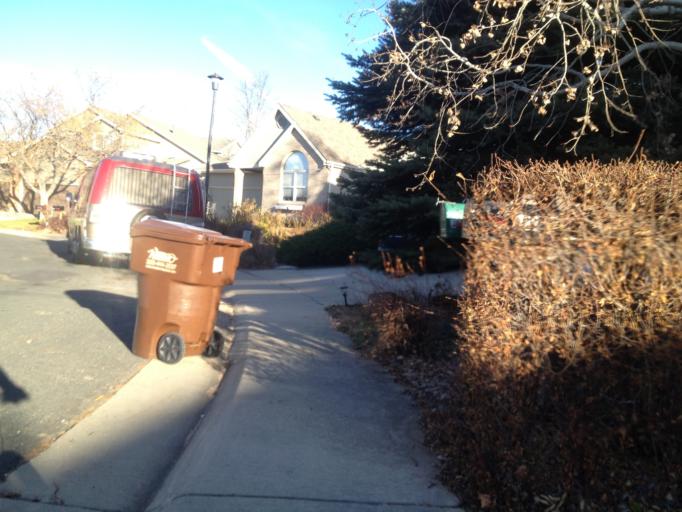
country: US
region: Colorado
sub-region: Boulder County
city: Superior
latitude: 39.9691
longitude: -105.1610
